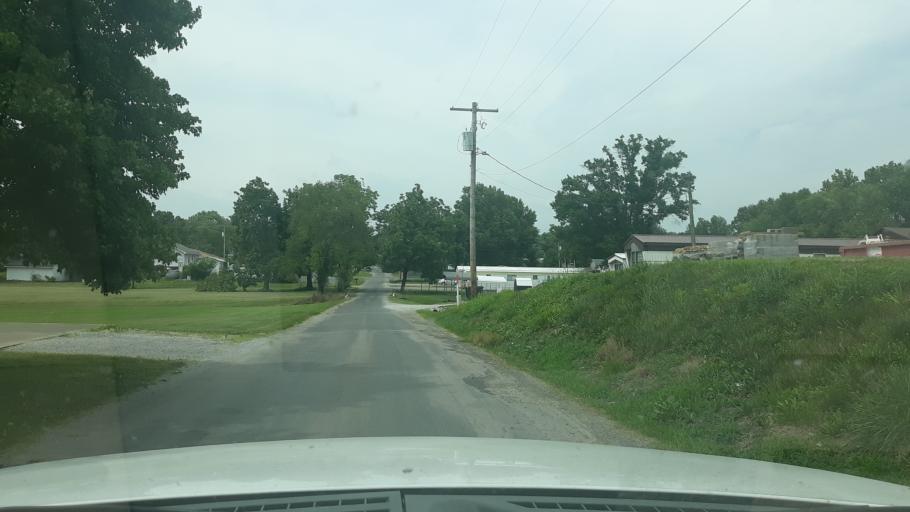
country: US
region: Illinois
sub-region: Saline County
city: Harrisburg
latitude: 37.8414
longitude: -88.6100
